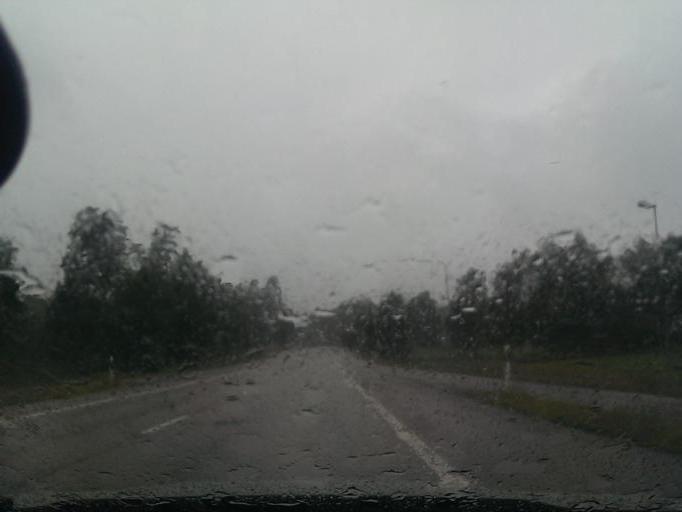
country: SE
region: Skane
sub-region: Orkelljunga Kommun
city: OErkelljunga
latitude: 56.2882
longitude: 13.3013
